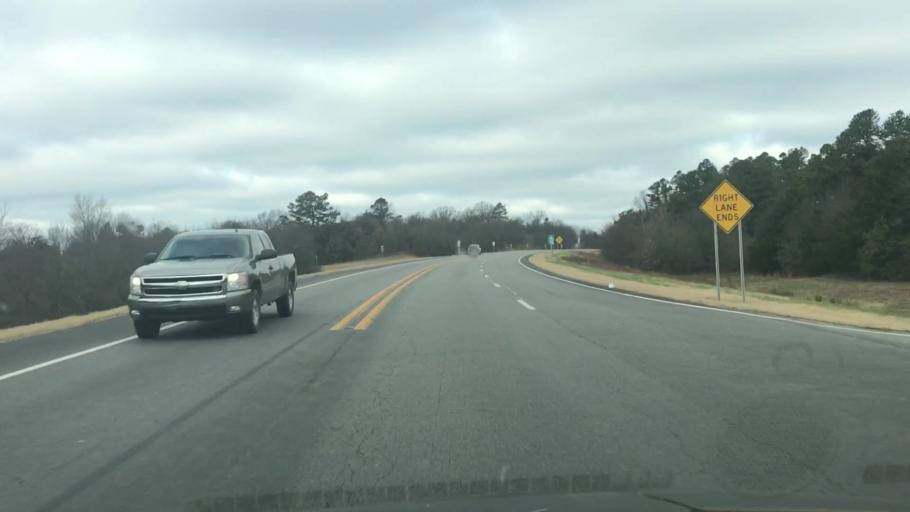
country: US
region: Arkansas
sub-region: Scott County
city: Waldron
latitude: 34.8819
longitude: -94.1035
